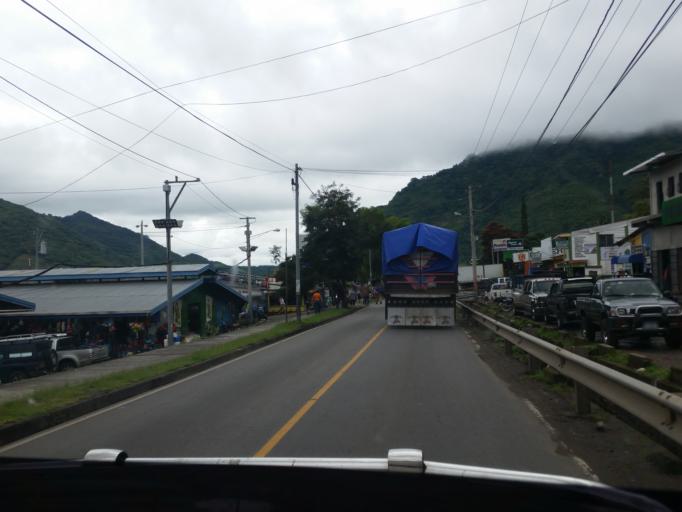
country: NI
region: Jinotega
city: Jinotega
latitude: 13.0949
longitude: -85.9963
